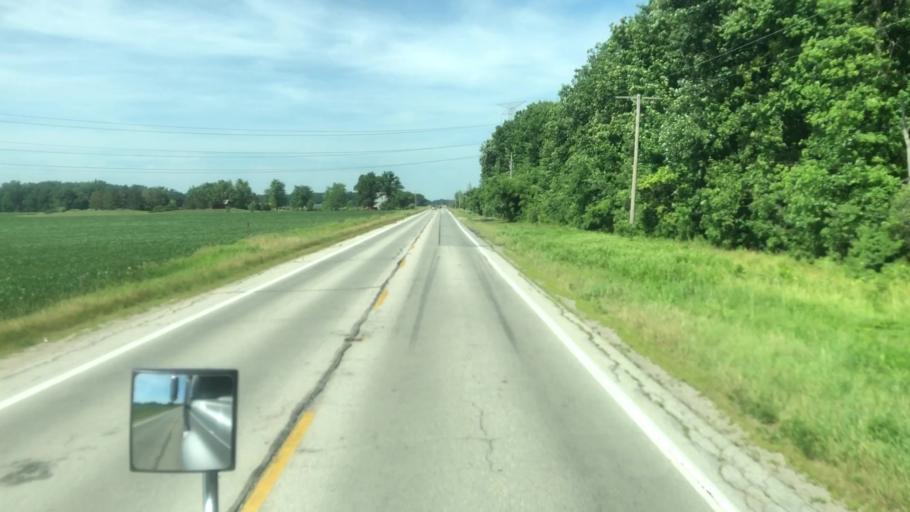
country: US
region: Ohio
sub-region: Sandusky County
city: Clyde
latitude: 41.4066
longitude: -82.9857
